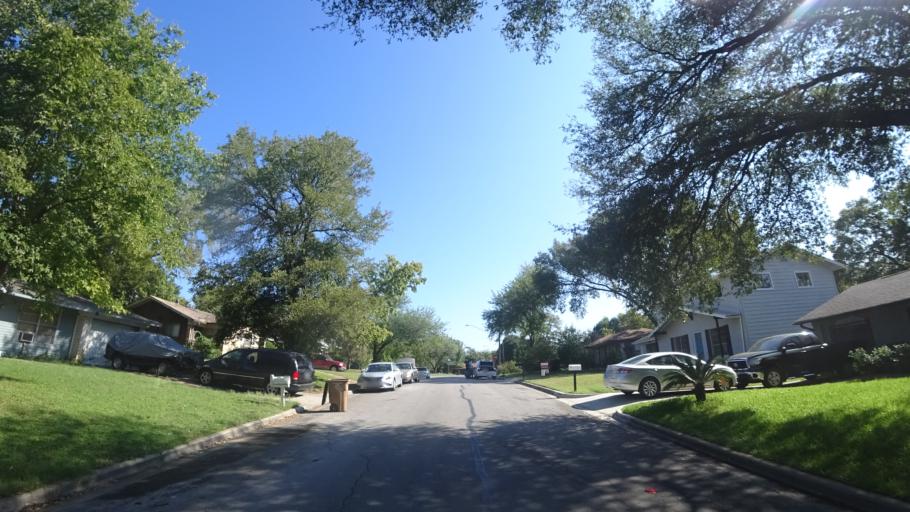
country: US
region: Texas
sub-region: Travis County
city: Austin
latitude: 30.3156
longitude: -97.6676
